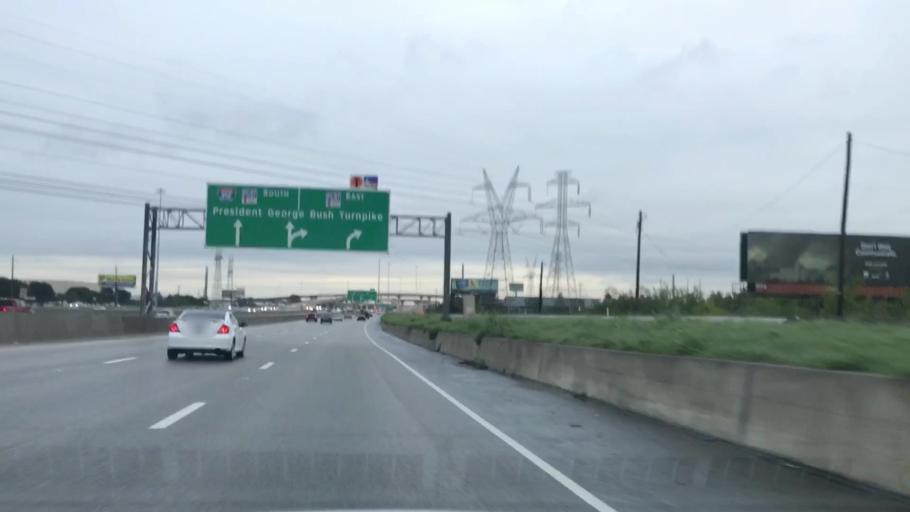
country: US
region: Texas
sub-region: Dallas County
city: Carrollton
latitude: 32.9902
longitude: -96.9428
